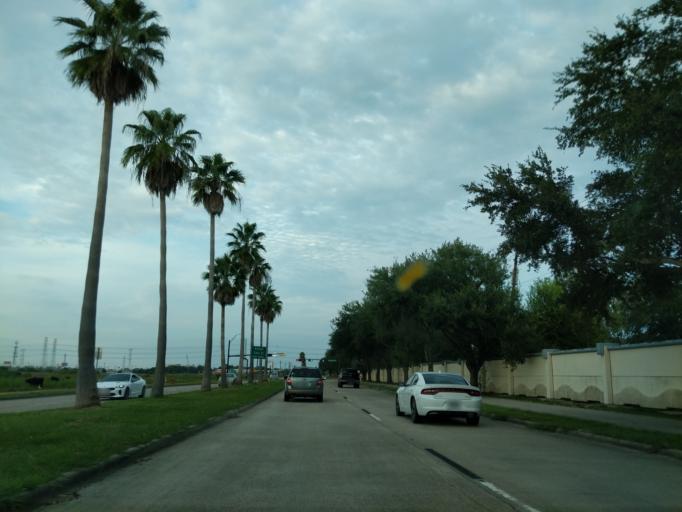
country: US
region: Texas
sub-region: Galveston County
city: Kemah
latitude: 29.5322
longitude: -95.0261
